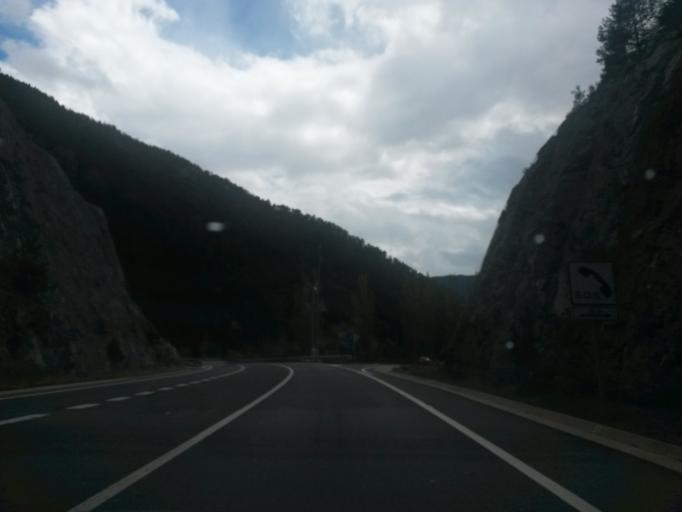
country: ES
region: Catalonia
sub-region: Provincia de Barcelona
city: Baga
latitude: 42.2724
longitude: 1.8537
